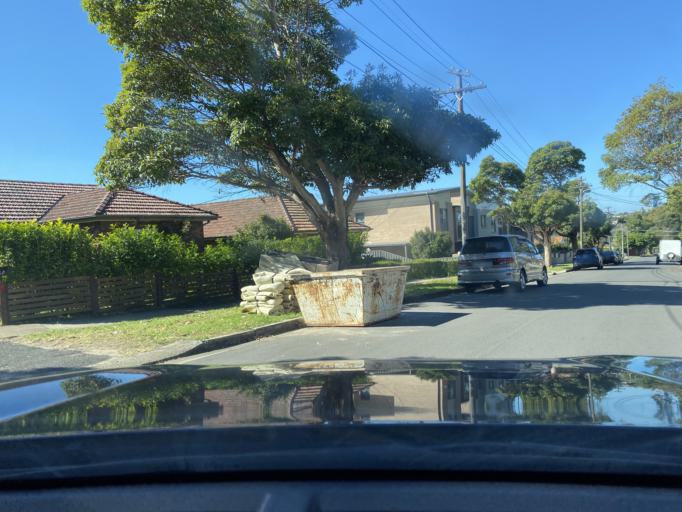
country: AU
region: New South Wales
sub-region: Canada Bay
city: Wareemba
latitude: -33.8526
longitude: 151.1325
